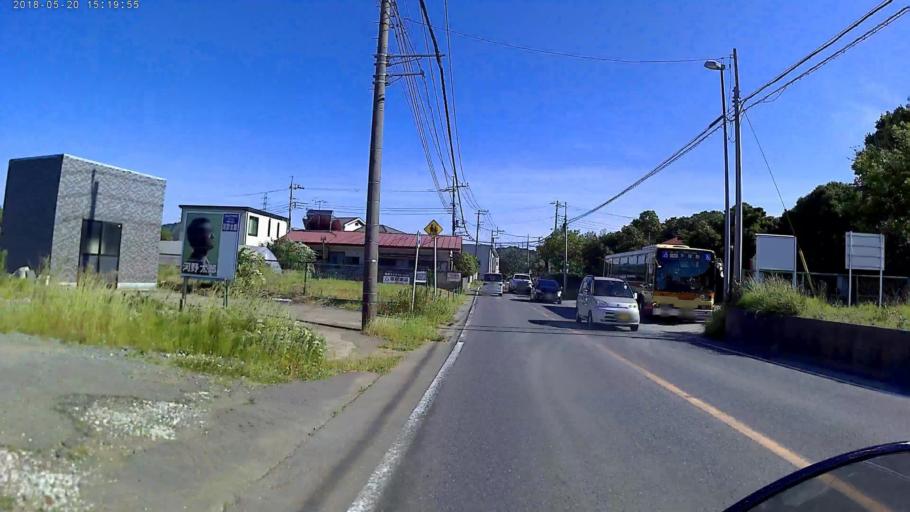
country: JP
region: Kanagawa
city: Oiso
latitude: 35.3383
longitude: 139.2928
